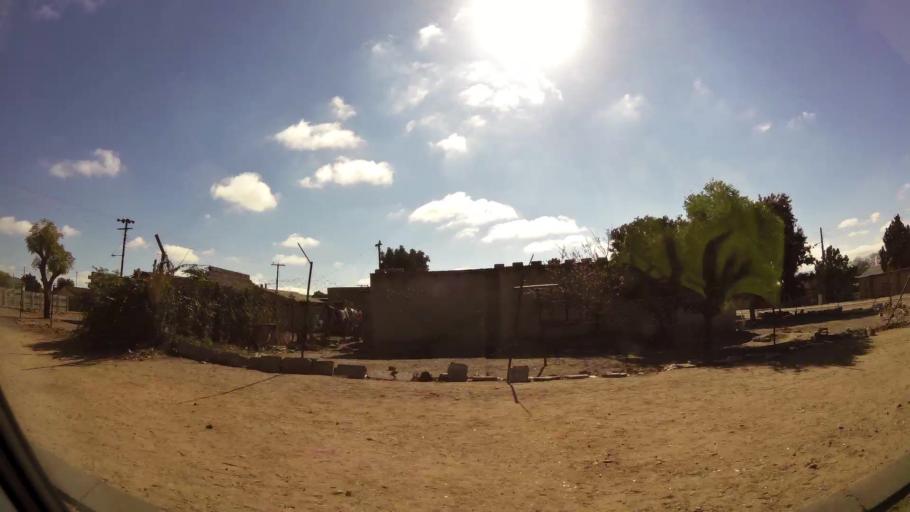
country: ZA
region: Limpopo
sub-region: Capricorn District Municipality
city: Polokwane
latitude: -23.8645
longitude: 29.3914
